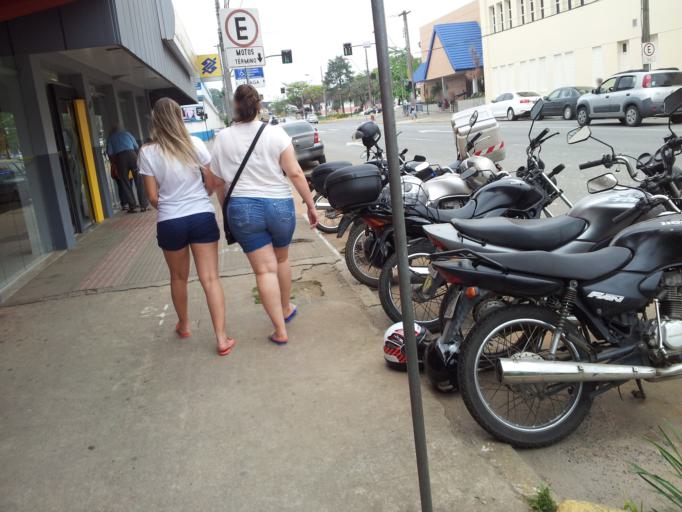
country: BR
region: Santa Catarina
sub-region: Joinville
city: Joinville
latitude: -26.3204
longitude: -48.8450
